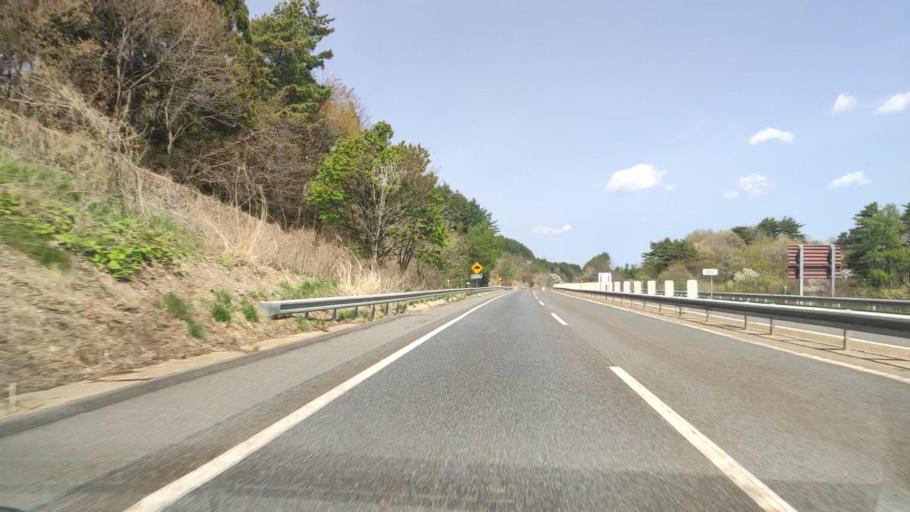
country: JP
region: Iwate
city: Ichinohe
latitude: 40.2628
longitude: 141.4003
